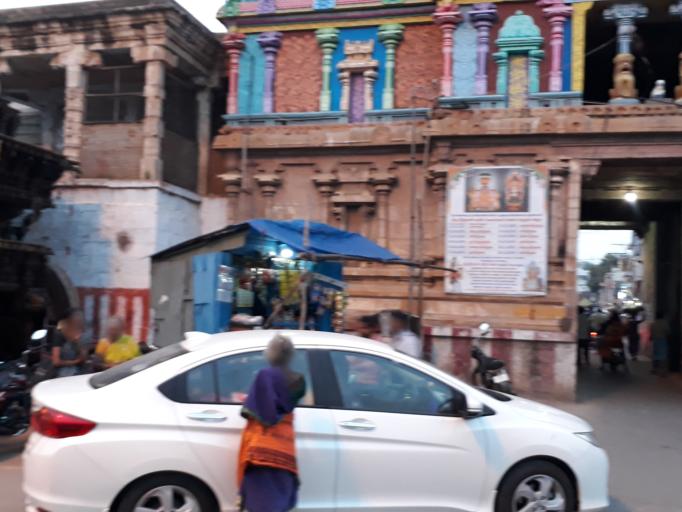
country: IN
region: Tamil Nadu
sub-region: Tiruchchirappalli
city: Tiruchirappalli
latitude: 10.8528
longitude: 78.7033
